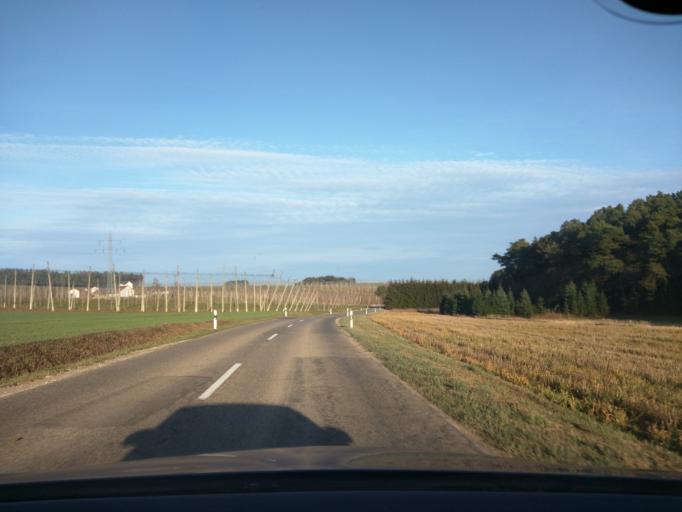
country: DE
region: Bavaria
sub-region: Upper Bavaria
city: Wolnzach
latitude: 48.5787
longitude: 11.6685
